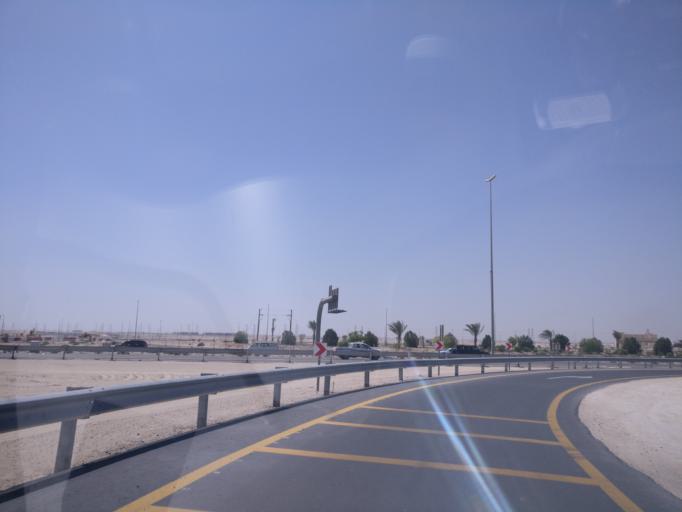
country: AE
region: Dubai
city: Dubai
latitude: 24.9121
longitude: 54.9595
